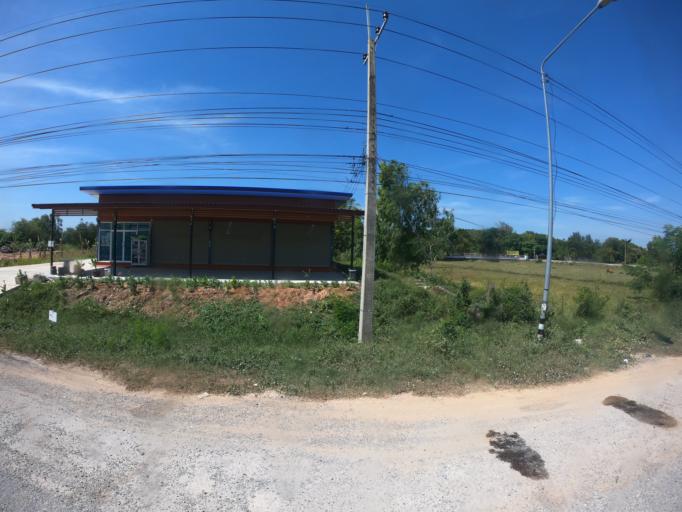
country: TH
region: Nakhon Ratchasima
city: Bua Lai
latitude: 15.6420
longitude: 102.5697
